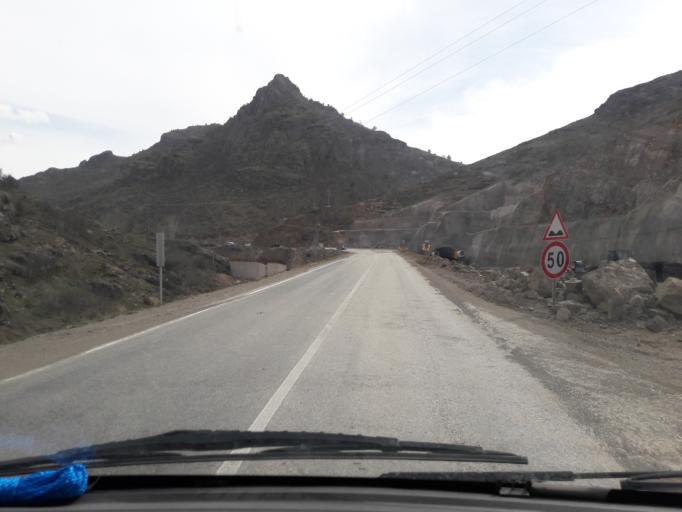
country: TR
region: Gumushane
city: Gumushkhane
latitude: 40.3012
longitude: 39.4738
